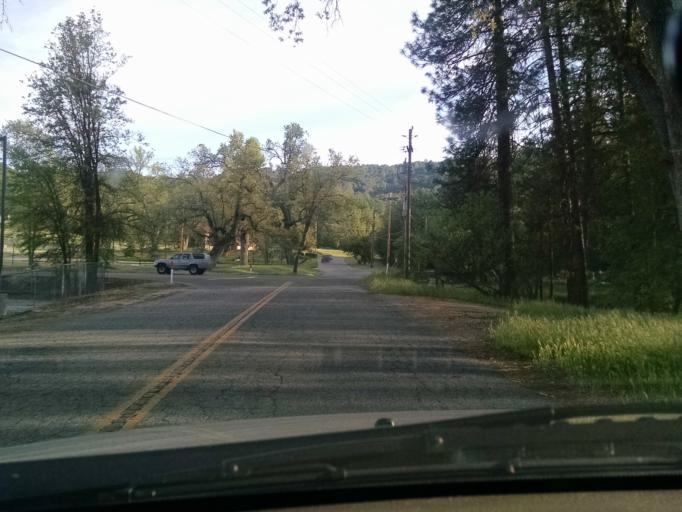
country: US
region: California
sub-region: Madera County
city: Oakhurst
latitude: 37.3292
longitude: -119.6266
